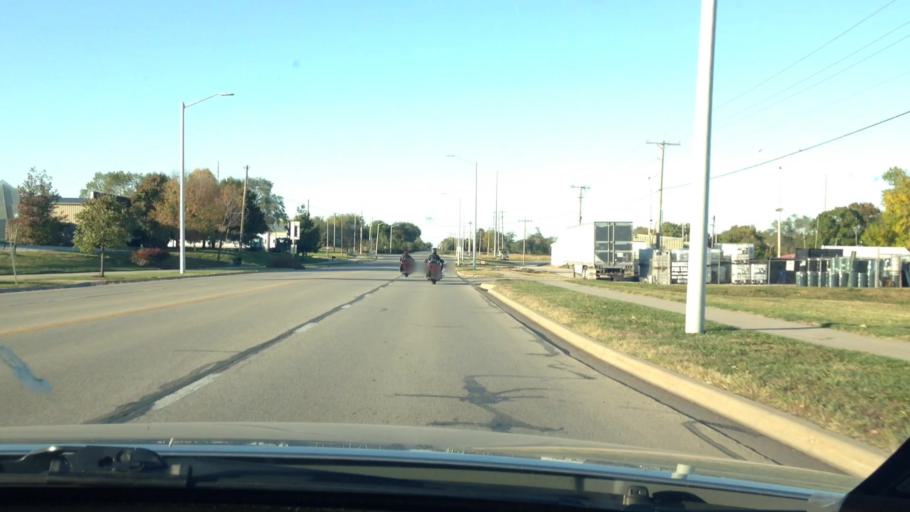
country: US
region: Kansas
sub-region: Johnson County
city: Gardner
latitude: 38.8229
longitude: -94.9276
